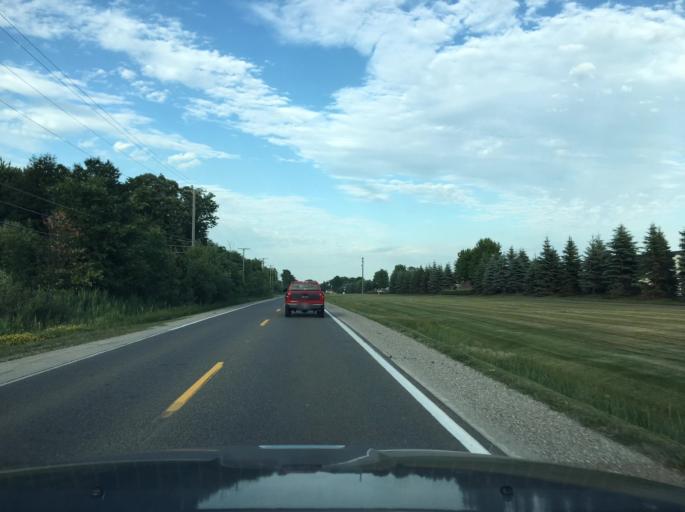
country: US
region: Michigan
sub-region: Macomb County
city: Shelby
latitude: 42.7166
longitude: -82.9356
